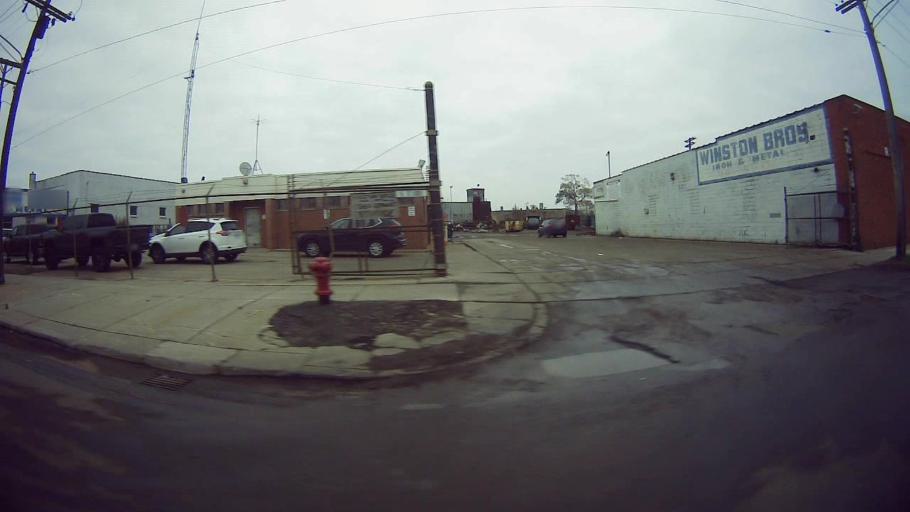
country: US
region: Michigan
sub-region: Wayne County
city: Hamtramck
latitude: 42.4215
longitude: -83.0655
